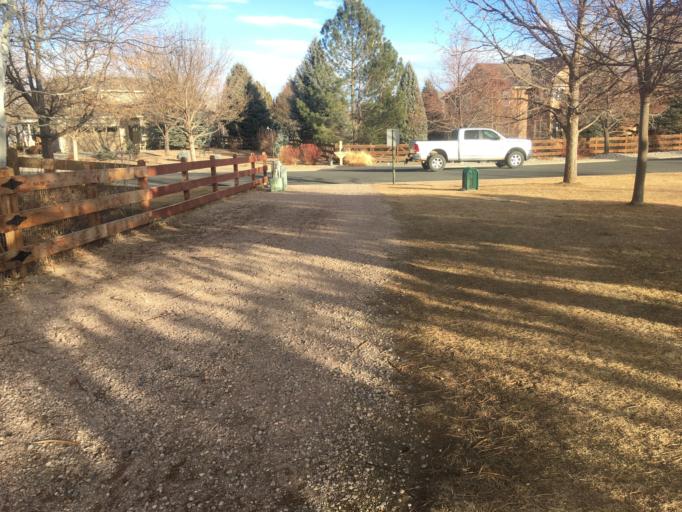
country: US
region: Colorado
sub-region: Boulder County
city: Lafayette
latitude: 40.0124
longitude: -105.0862
